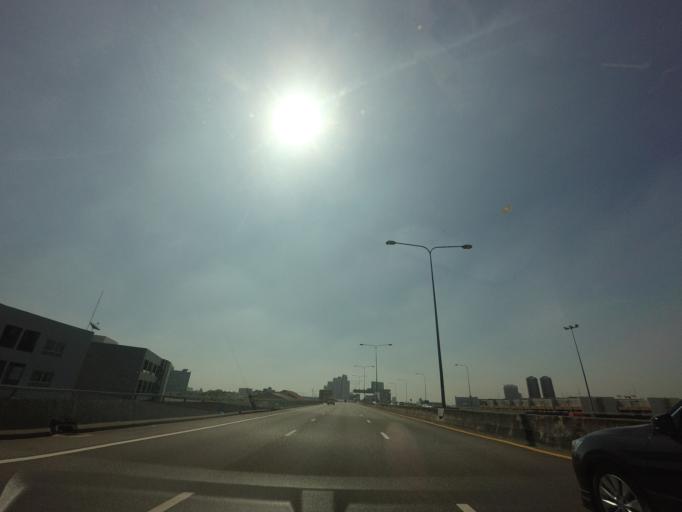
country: TH
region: Bangkok
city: Phra Khanong
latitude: 13.6842
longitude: 100.6028
